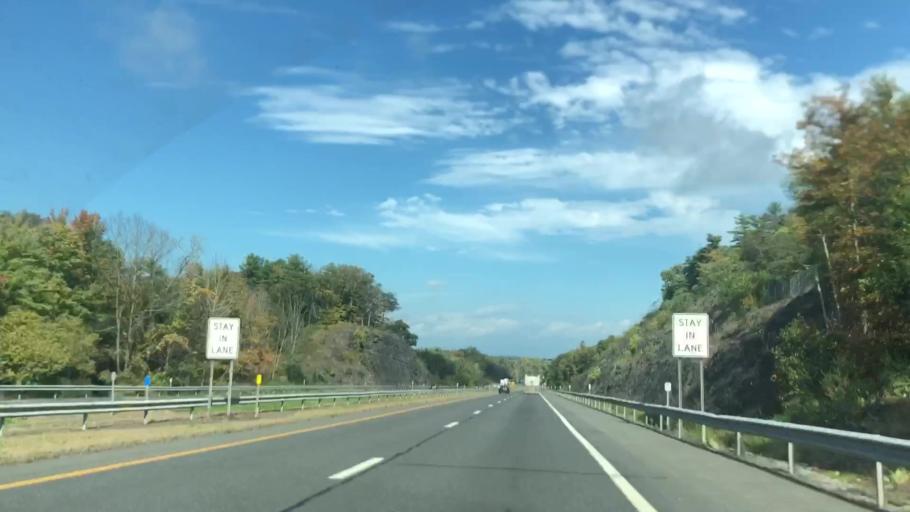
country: US
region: New York
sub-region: Ulster County
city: Tillson
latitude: 41.8095
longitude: -74.0531
